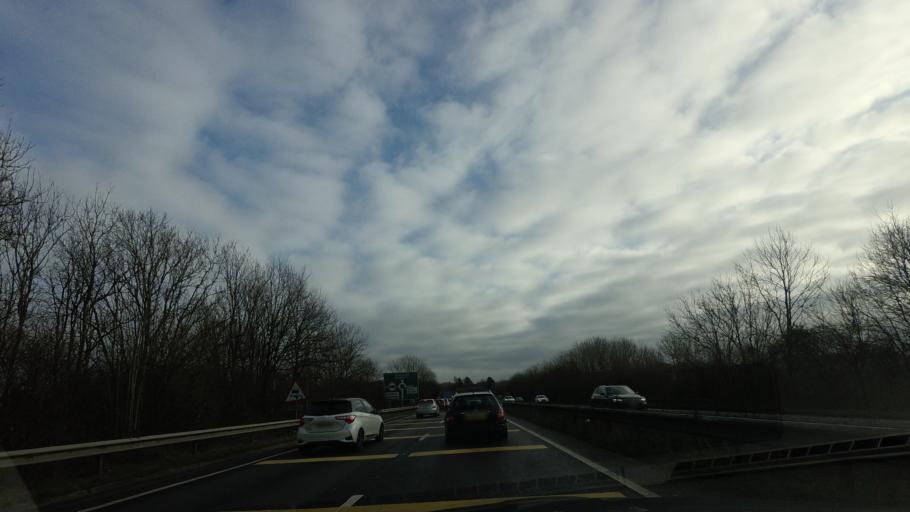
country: GB
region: England
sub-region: Kent
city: Pembury
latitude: 51.1365
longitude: 0.3463
